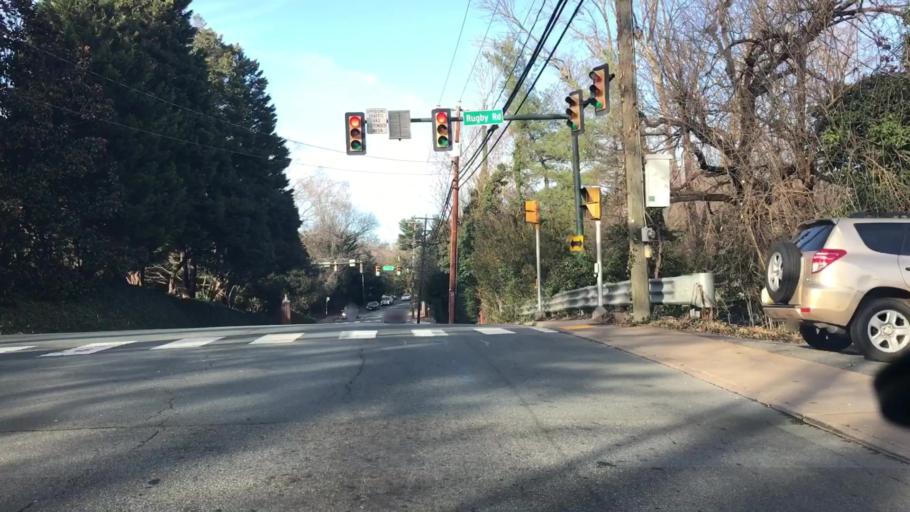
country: US
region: Virginia
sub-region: City of Charlottesville
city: Charlottesville
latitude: 38.0456
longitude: -78.4931
